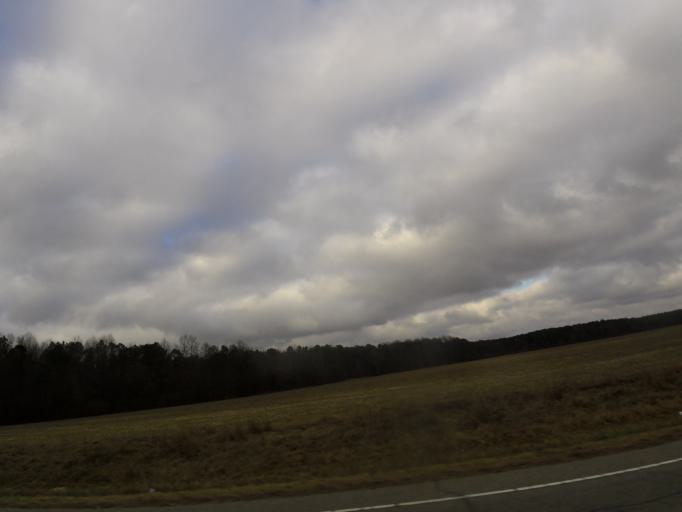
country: US
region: North Carolina
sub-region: Edgecombe County
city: Pinetops
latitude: 35.8583
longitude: -77.6940
